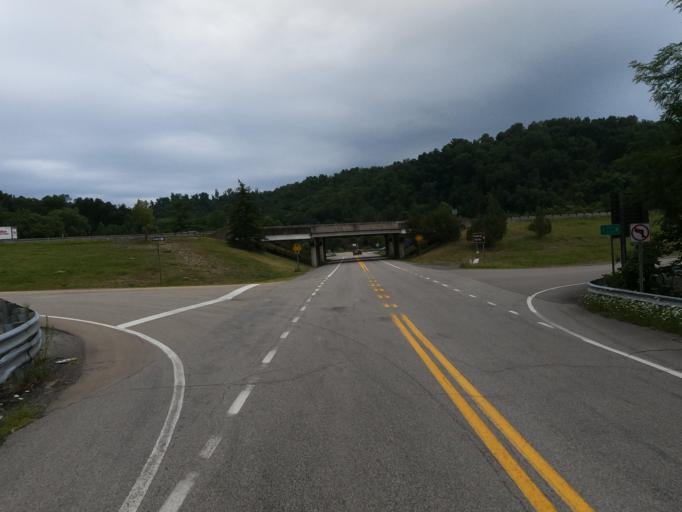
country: US
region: West Virginia
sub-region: Marion County
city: Fairmont
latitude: 39.4900
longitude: -80.0894
